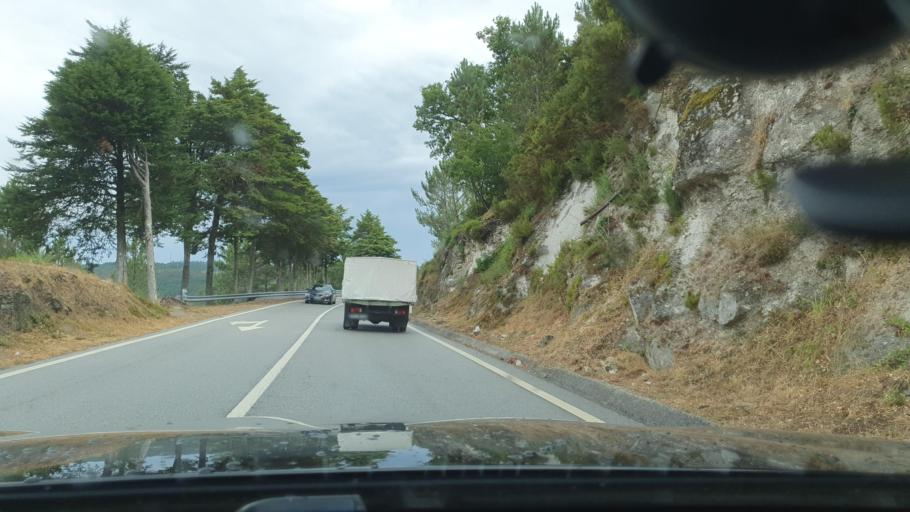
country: PT
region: Braga
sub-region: Cabeceiras de Basto
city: Cabeceiras de Basto
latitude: 41.6717
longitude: -7.9818
